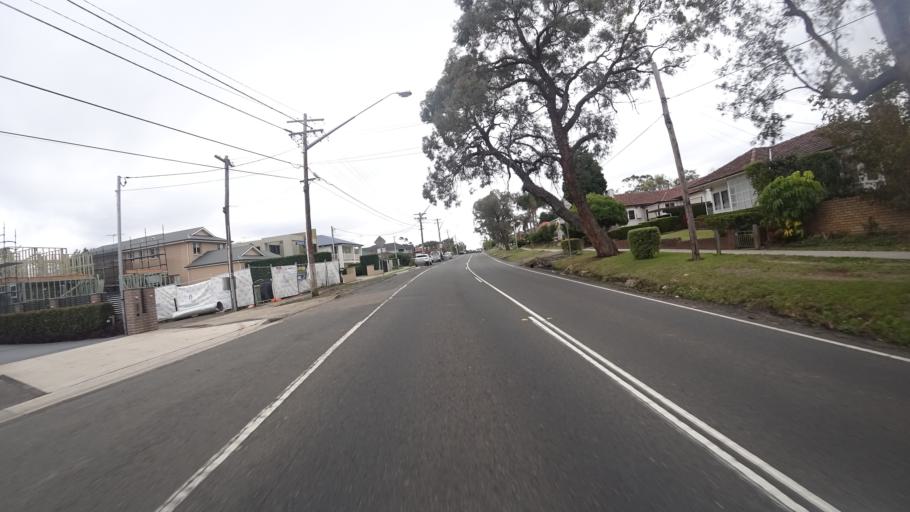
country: AU
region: New South Wales
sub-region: Liverpool
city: East Hills
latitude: -33.9607
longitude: 150.9820
